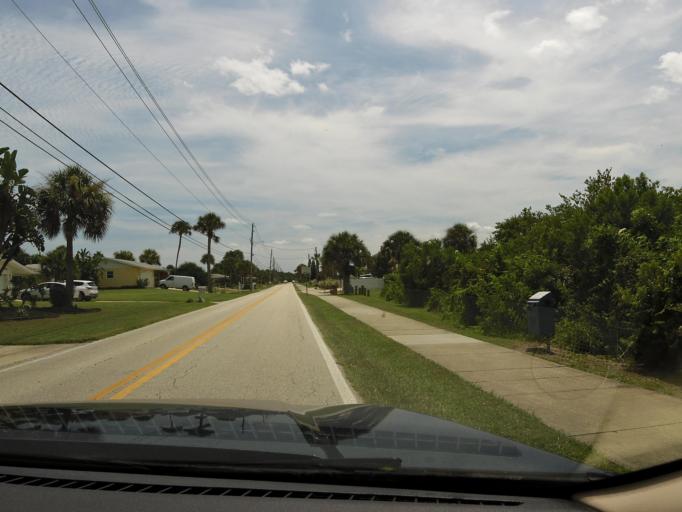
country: US
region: Florida
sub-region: Volusia County
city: Ponce Inlet
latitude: 29.1197
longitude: -80.9533
